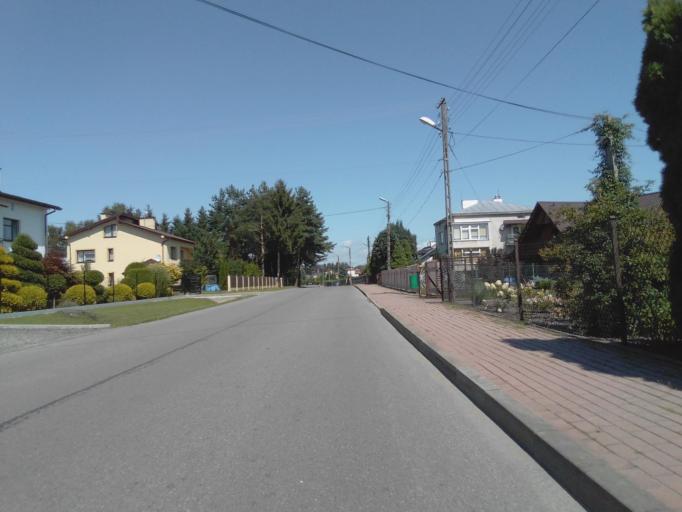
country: PL
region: Subcarpathian Voivodeship
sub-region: Powiat krosnienski
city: Jedlicze
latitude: 49.7167
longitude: 21.6373
